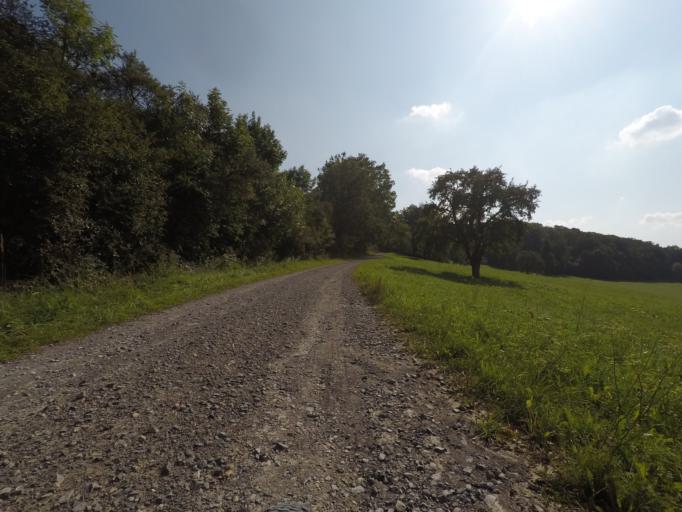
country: DE
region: Baden-Wuerttemberg
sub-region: Regierungsbezirk Stuttgart
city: Weil im Schonbuch
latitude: 48.6379
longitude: 9.0679
